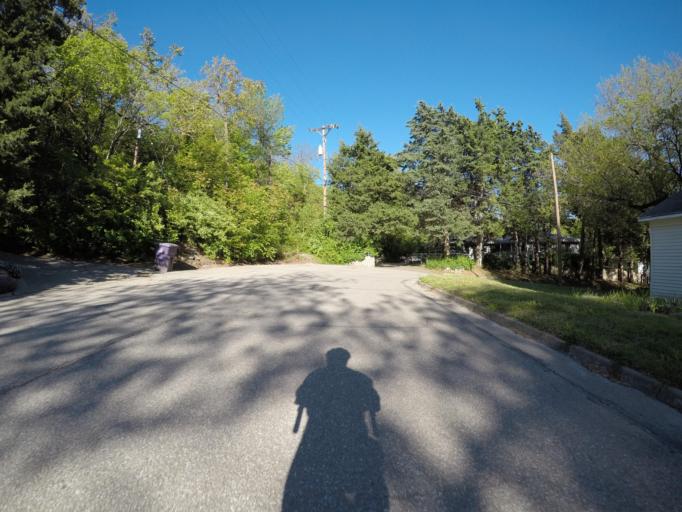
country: US
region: Kansas
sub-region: Riley County
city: Manhattan
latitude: 39.1933
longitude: -96.5697
